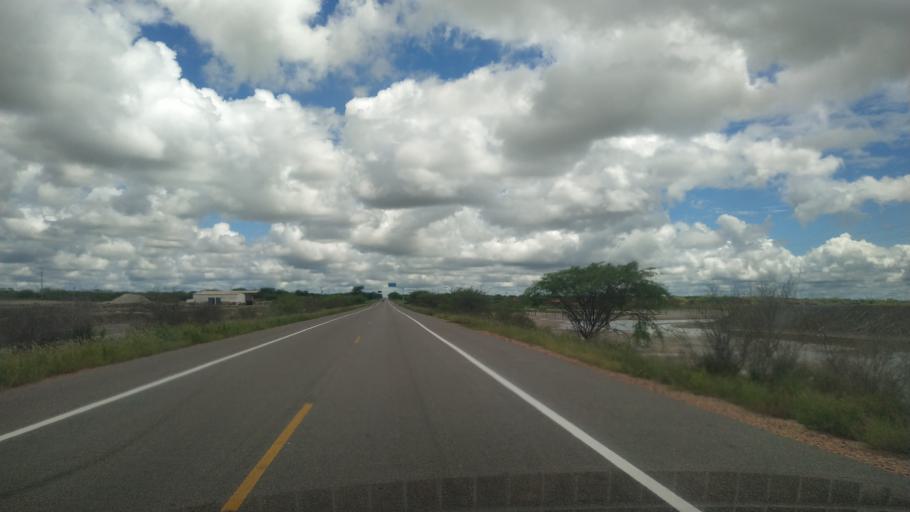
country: BR
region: Rio Grande do Norte
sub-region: Areia Branca
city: Areia Branca
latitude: -5.0527
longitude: -37.1507
